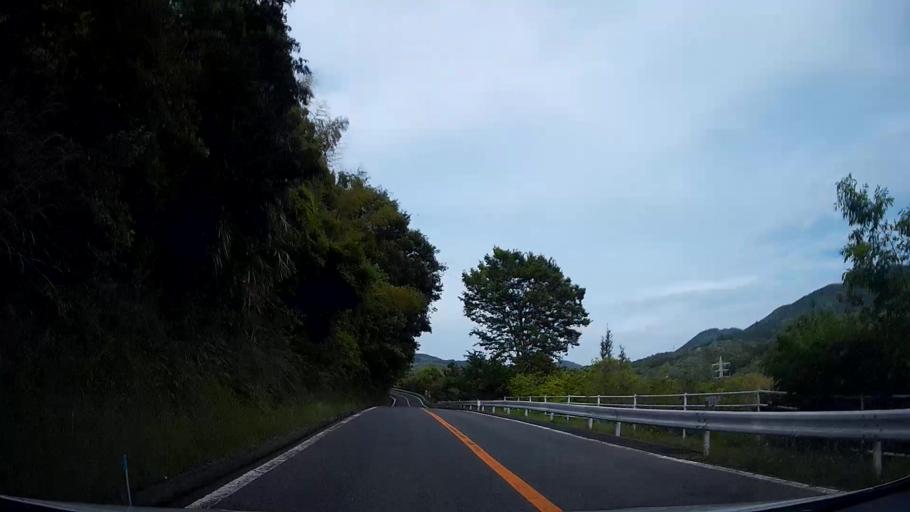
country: JP
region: Shizuoka
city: Ito
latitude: 34.9495
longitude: 139.0298
